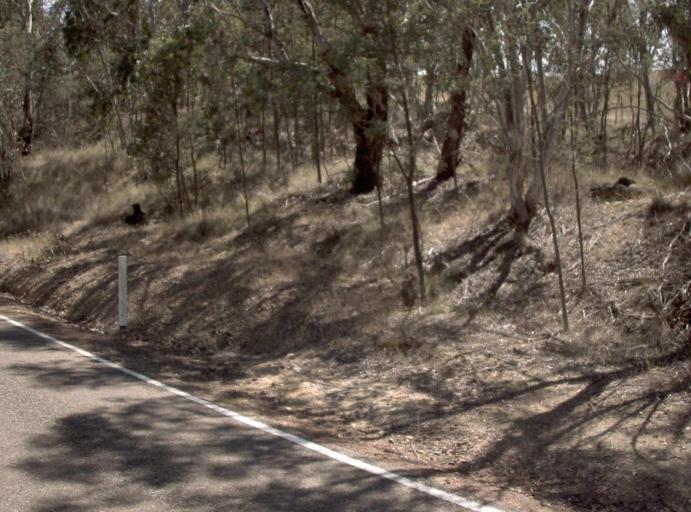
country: AU
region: Victoria
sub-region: Alpine
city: Mount Beauty
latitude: -37.0442
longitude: 147.6227
